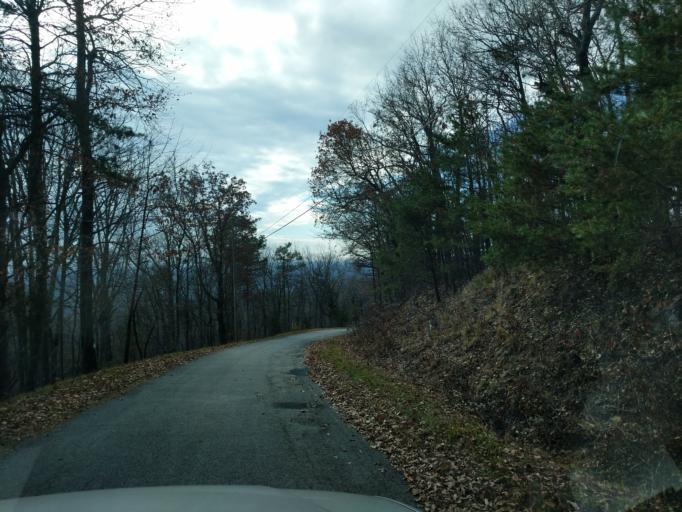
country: US
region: South Carolina
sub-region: Pickens County
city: Pickens
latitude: 34.8990
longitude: -82.6594
